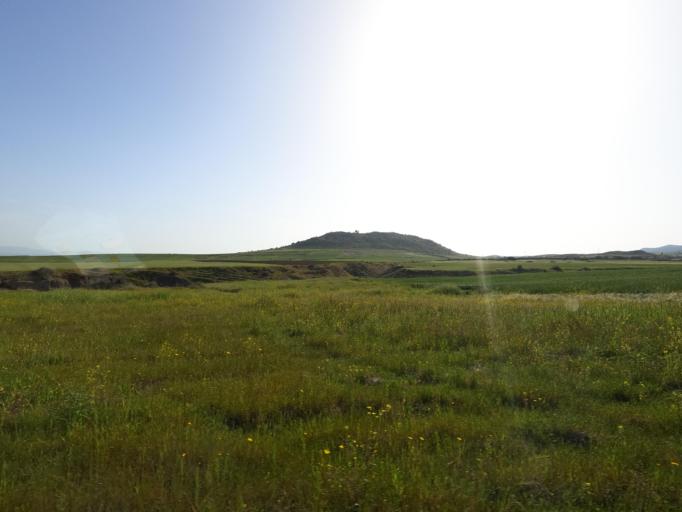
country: CY
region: Lefkosia
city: Lefka
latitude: 35.0917
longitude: 32.9444
